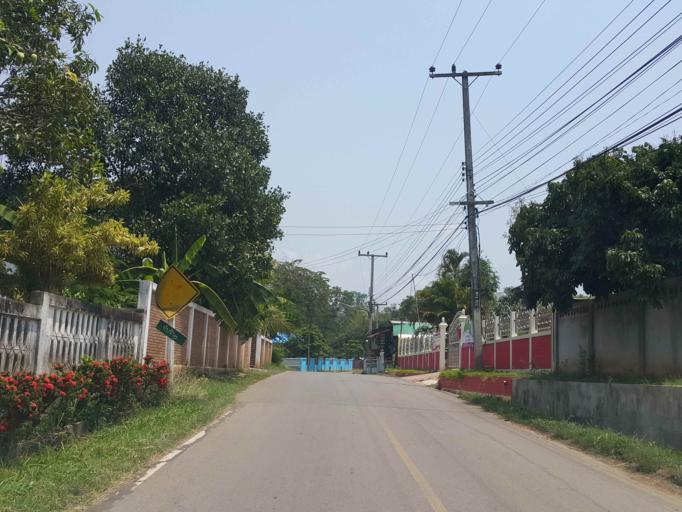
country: TH
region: Chiang Mai
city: Mae Taeng
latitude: 19.1510
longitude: 98.8586
